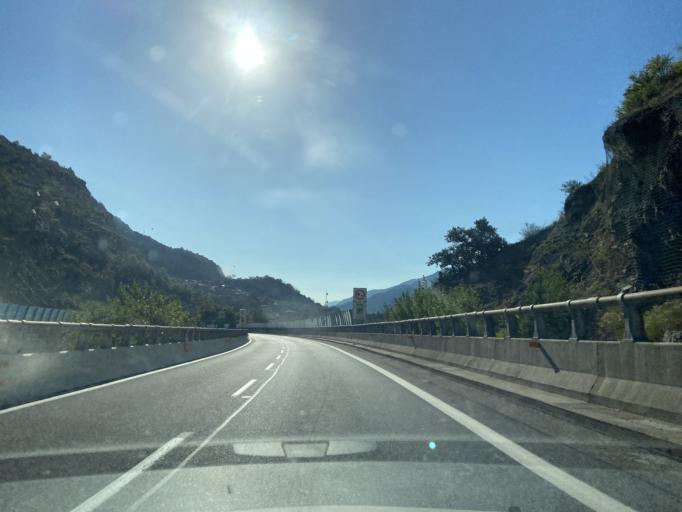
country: IT
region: Piedmont
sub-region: Provincia di Torino
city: Susa
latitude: 45.1423
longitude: 7.0542
